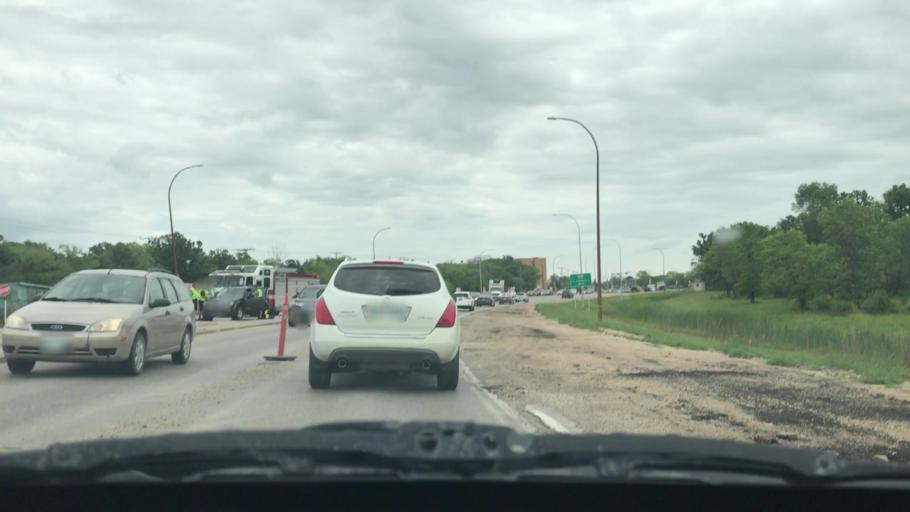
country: CA
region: Manitoba
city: Winnipeg
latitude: 49.8579
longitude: -97.0935
